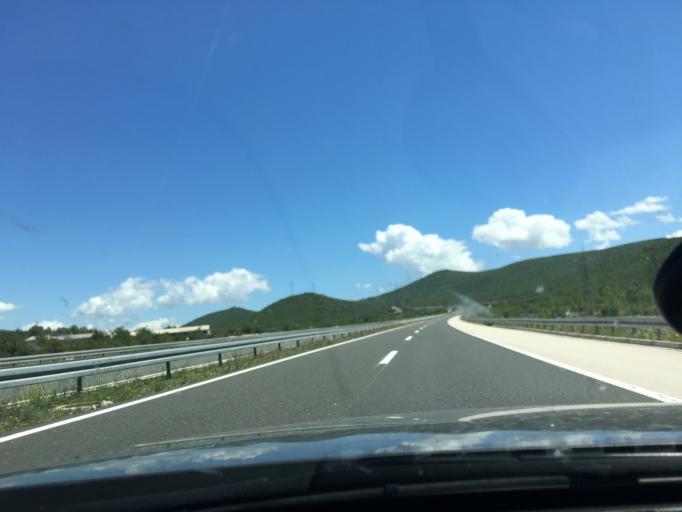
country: HR
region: Splitsko-Dalmatinska
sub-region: Grad Trogir
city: Trogir
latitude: 43.6721
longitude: 16.1605
